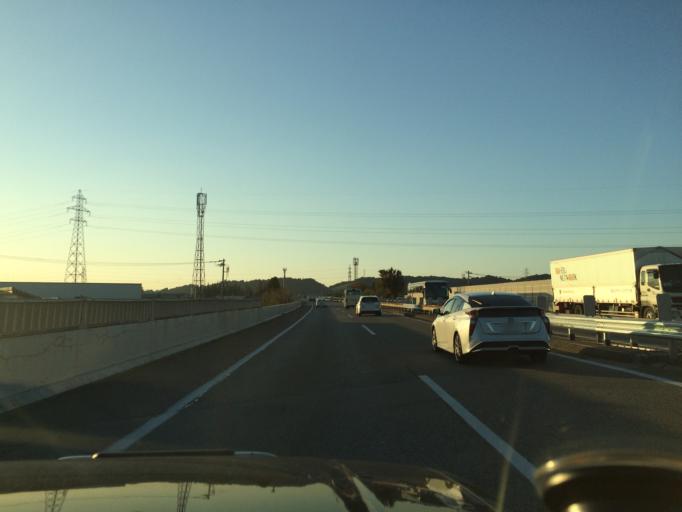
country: JP
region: Toyama
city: Toyama-shi
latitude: 36.6730
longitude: 137.1739
